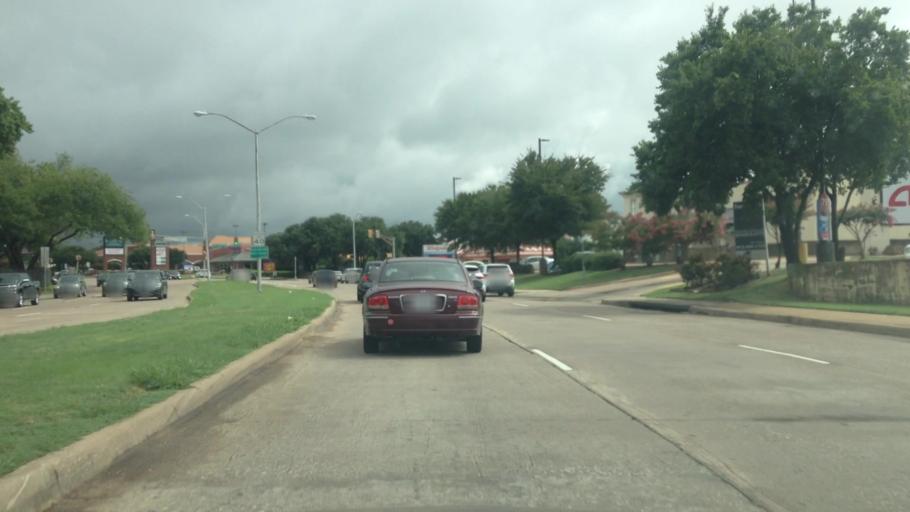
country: US
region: Texas
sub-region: Tarrant County
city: Benbrook
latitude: 32.6626
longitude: -97.4025
